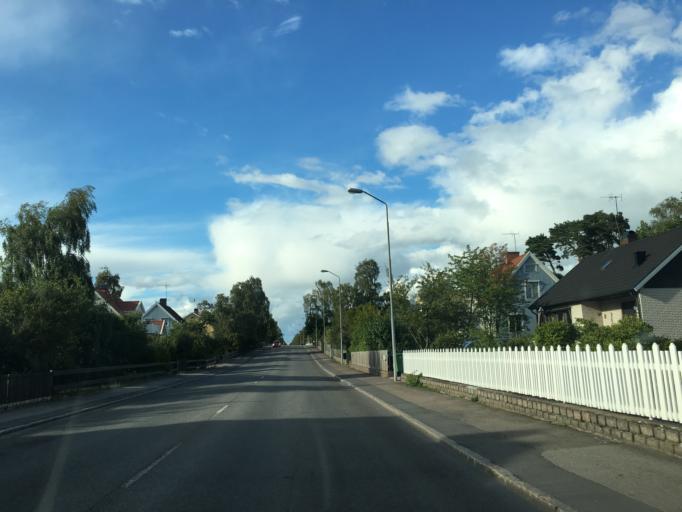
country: SE
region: Kalmar
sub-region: Kalmar Kommun
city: Kalmar
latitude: 56.6890
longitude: 16.3557
